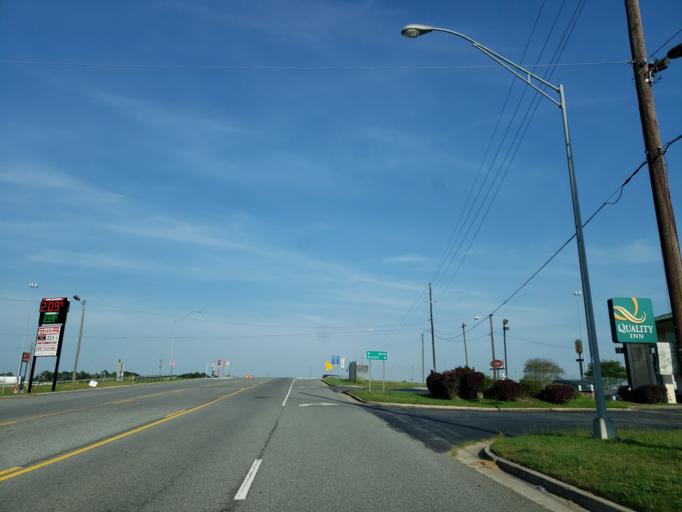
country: US
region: Georgia
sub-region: Tift County
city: Tifton
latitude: 31.4580
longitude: -83.5320
